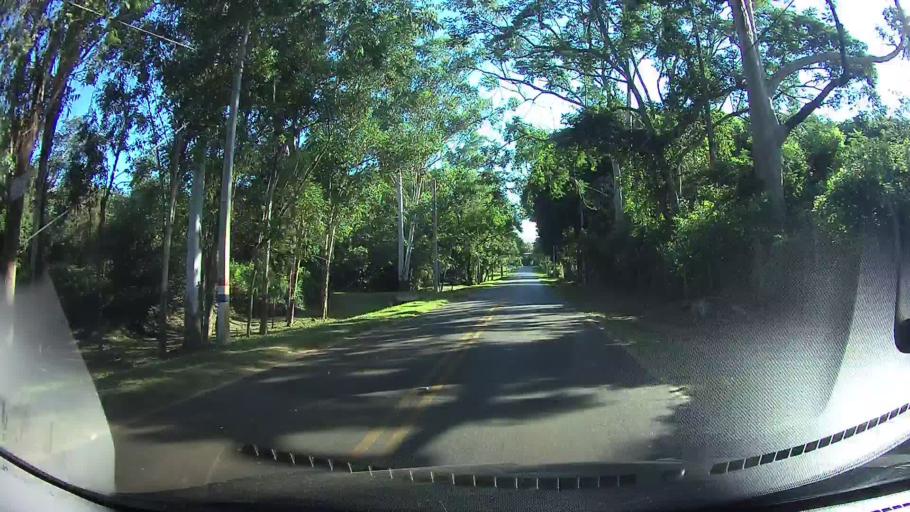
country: PY
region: Cordillera
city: Atyra
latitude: -25.2862
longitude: -57.1781
